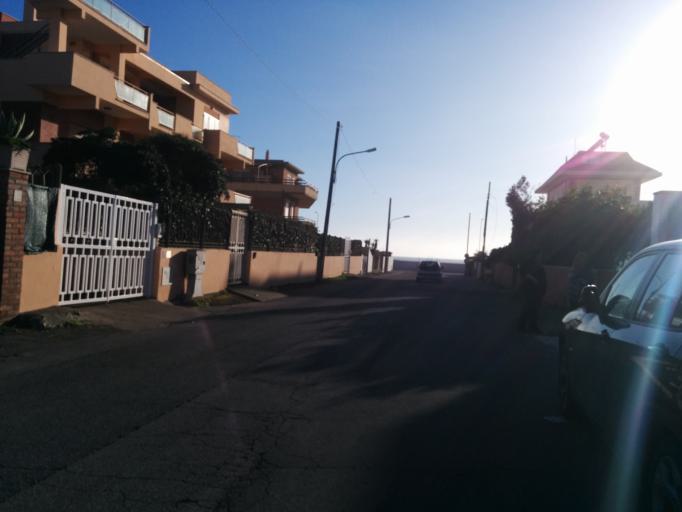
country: IT
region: Latium
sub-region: Citta metropolitana di Roma Capitale
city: Lavinio
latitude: 41.4962
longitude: 12.5872
